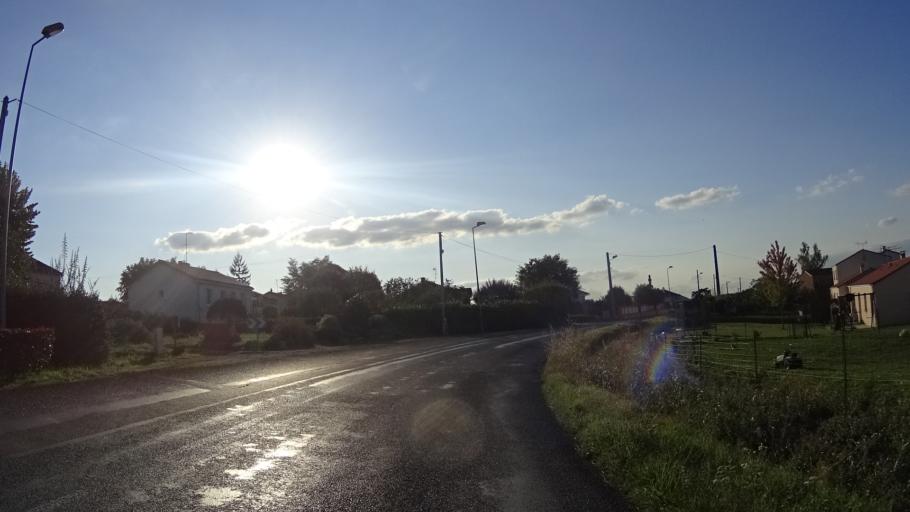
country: FR
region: Pays de la Loire
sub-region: Departement de Maine-et-Loire
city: Lire
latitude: 47.3432
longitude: -1.1531
